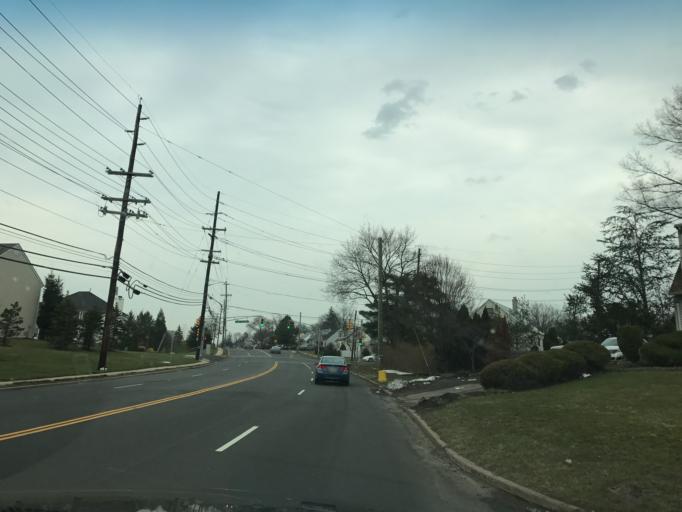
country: US
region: New Jersey
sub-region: Middlesex County
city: East Brunswick
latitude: 40.4407
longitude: -74.4054
